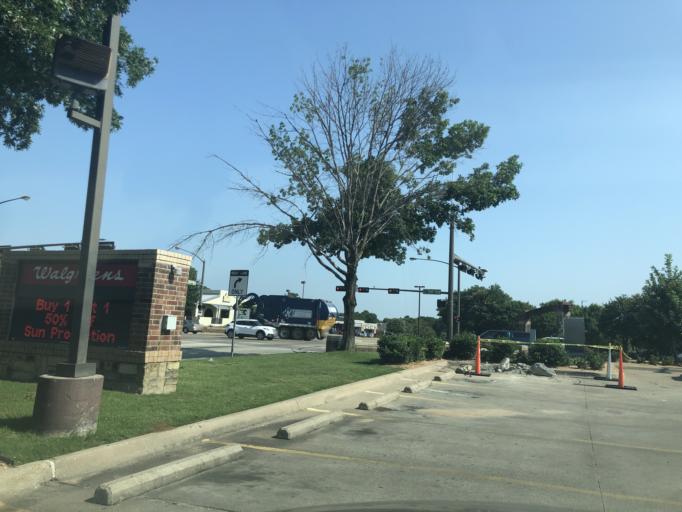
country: US
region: Texas
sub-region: Dallas County
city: Irving
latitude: 32.8007
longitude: -96.9589
